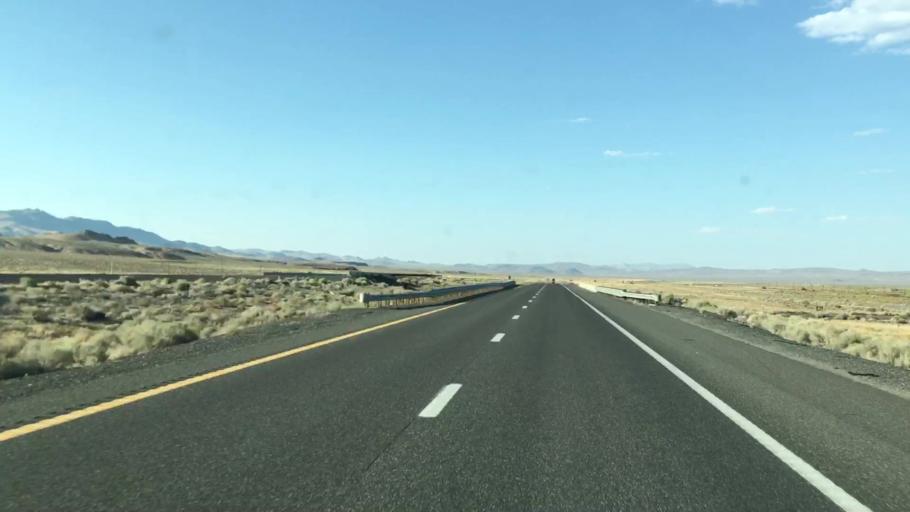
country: US
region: Nevada
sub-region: Pershing County
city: Lovelock
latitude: 40.0097
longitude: -118.6771
